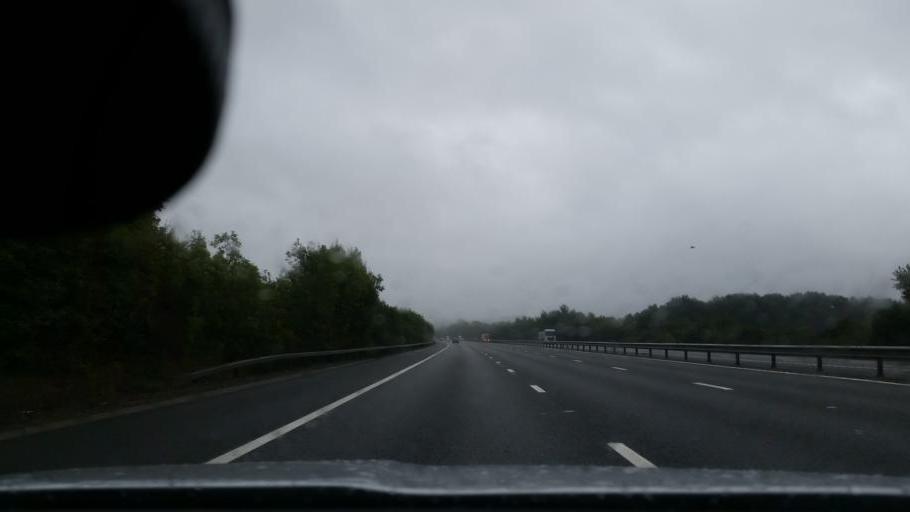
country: GB
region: England
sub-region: Kent
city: Borough Green
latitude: 51.3094
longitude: 0.3222
